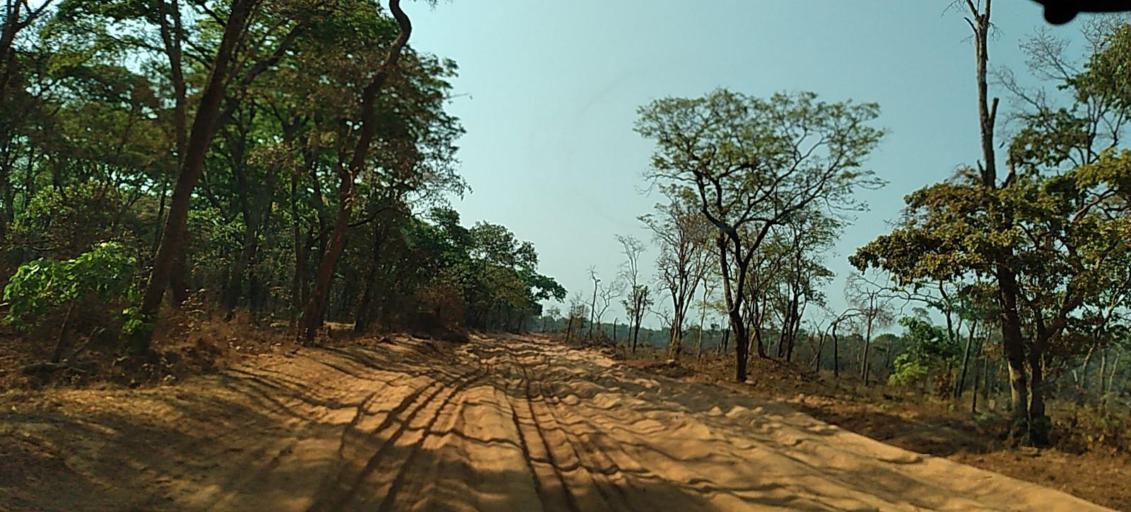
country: ZM
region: North-Western
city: Kasempa
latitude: -13.6342
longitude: 25.9912
